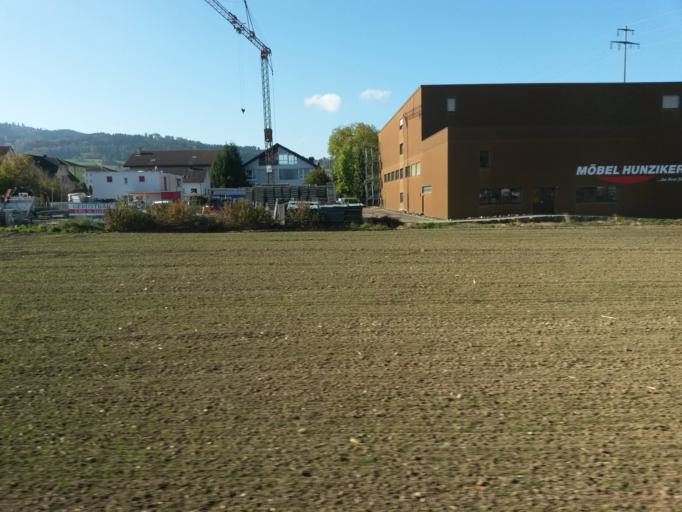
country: CH
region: Aargau
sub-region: Bezirk Kulm
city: Reinach
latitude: 47.2631
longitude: 8.1785
